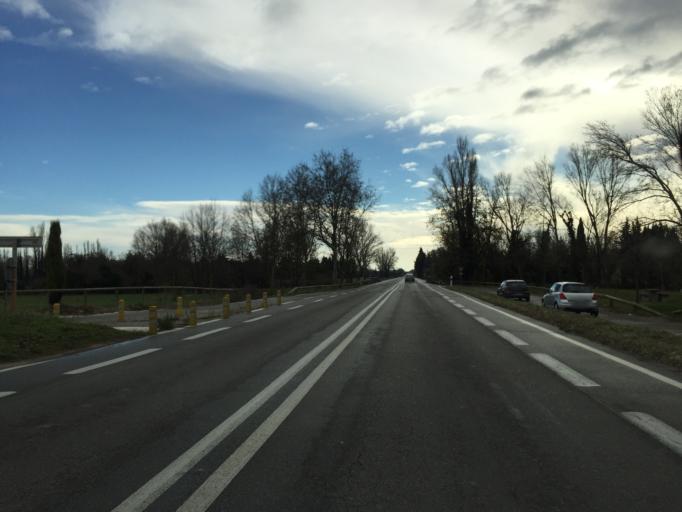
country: FR
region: Provence-Alpes-Cote d'Azur
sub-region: Departement du Vaucluse
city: Velleron
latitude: 43.9510
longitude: 5.0271
